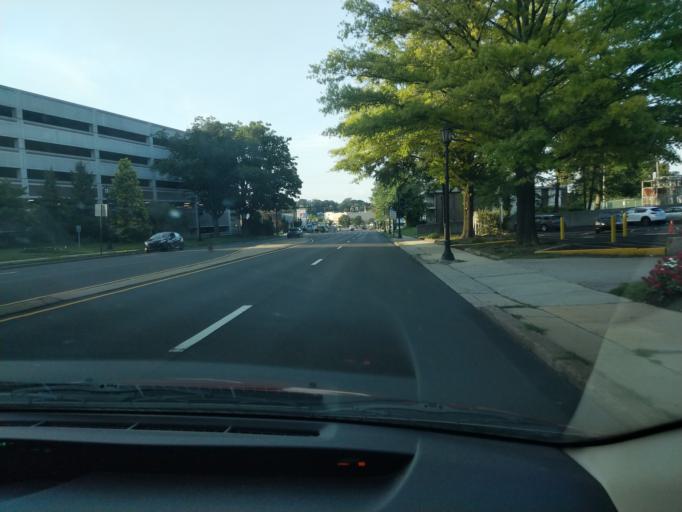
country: US
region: Pennsylvania
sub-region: Montgomery County
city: Willow Grove
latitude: 40.1199
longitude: -75.1188
